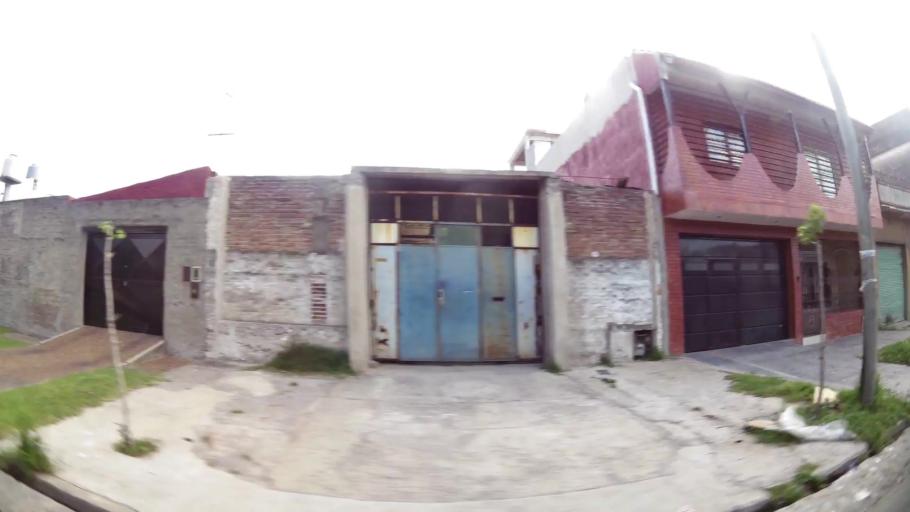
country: AR
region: Buenos Aires
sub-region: Partido de Avellaneda
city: Avellaneda
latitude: -34.6834
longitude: -58.3584
